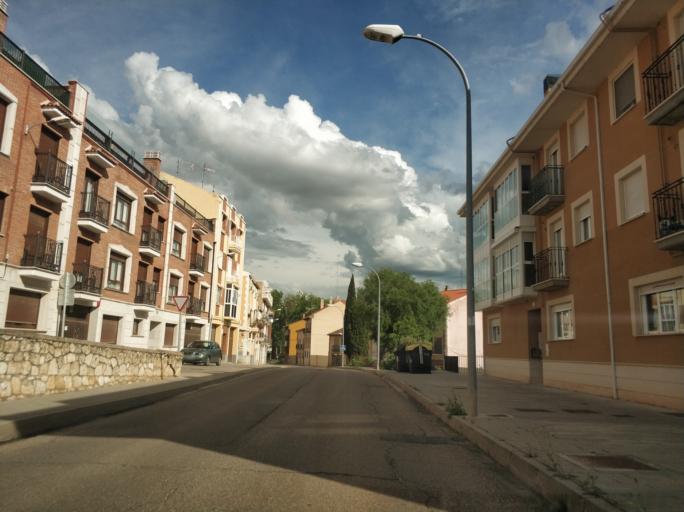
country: ES
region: Castille and Leon
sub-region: Provincia de Burgos
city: Aranda de Duero
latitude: 41.6729
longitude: -3.6932
